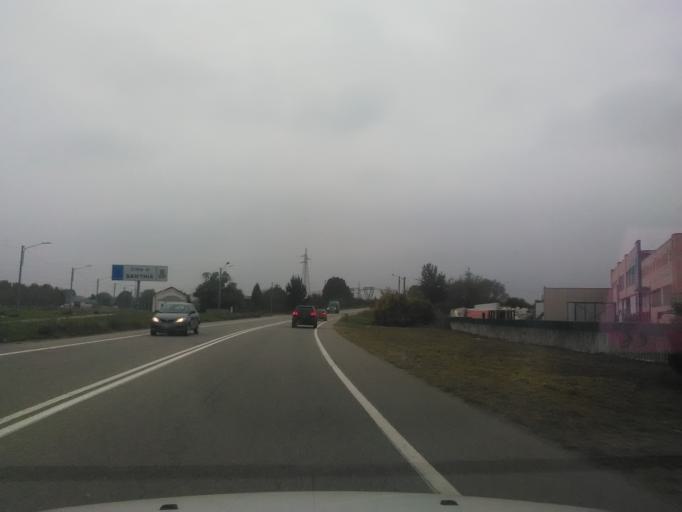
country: IT
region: Piedmont
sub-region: Provincia di Vercelli
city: Santhia
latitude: 45.3627
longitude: 8.1896
